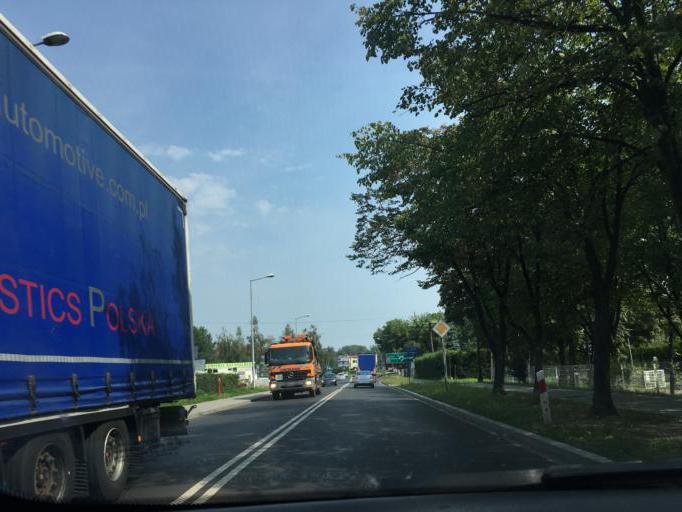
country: PL
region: Lesser Poland Voivodeship
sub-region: Powiat oswiecimski
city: Oswiecim
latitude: 50.0395
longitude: 19.2135
